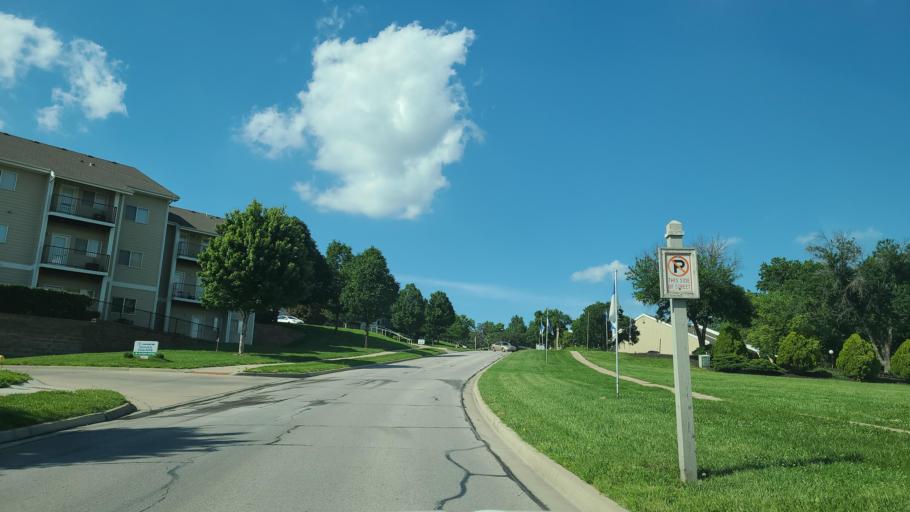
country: US
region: Kansas
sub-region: Douglas County
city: Lawrence
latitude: 38.9578
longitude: -95.2672
